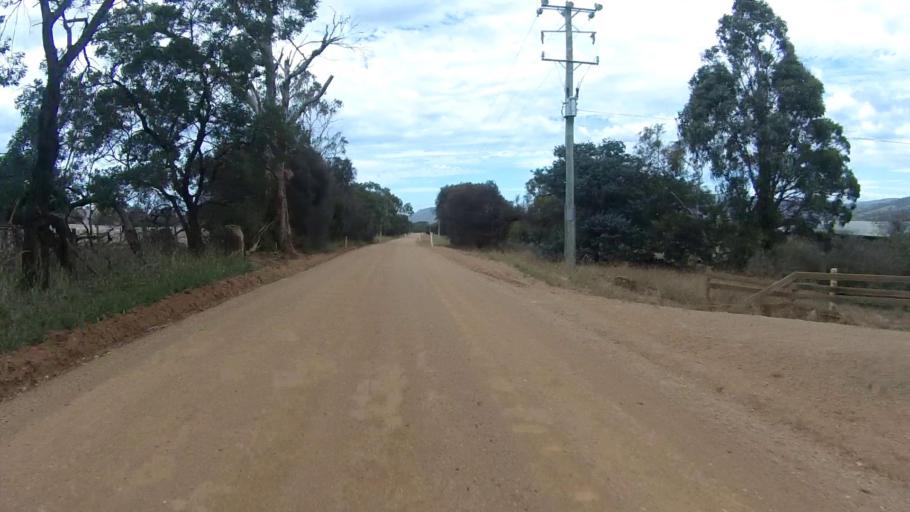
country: AU
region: Tasmania
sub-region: Clarence
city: Cambridge
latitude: -42.7061
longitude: 147.4567
